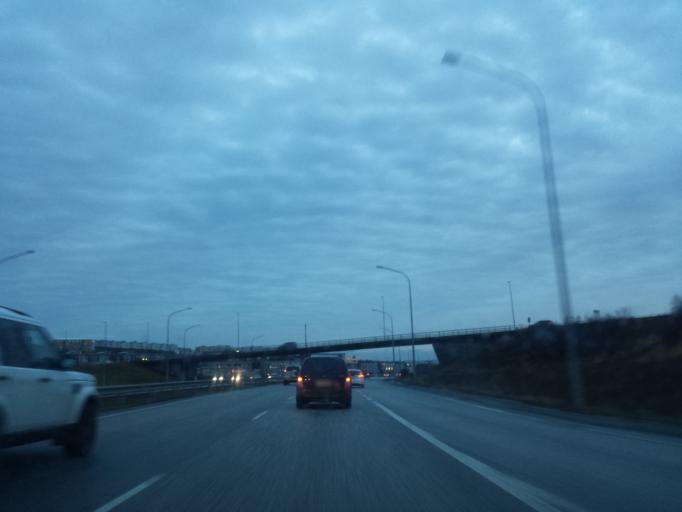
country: IS
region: Capital Region
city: Mosfellsbaer
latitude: 64.1338
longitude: -21.7626
